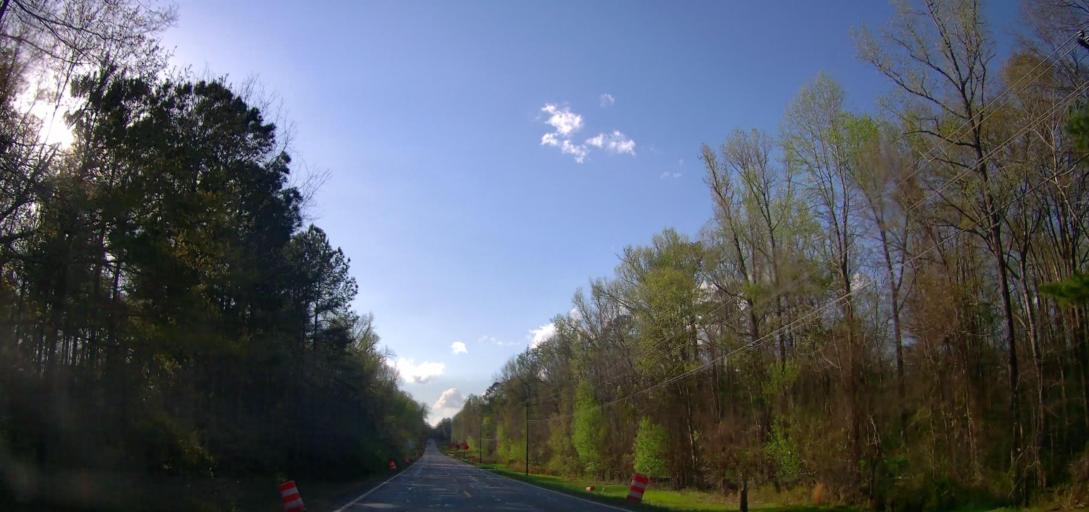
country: US
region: Georgia
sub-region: Putnam County
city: Eatonton
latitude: 33.1729
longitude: -83.3949
